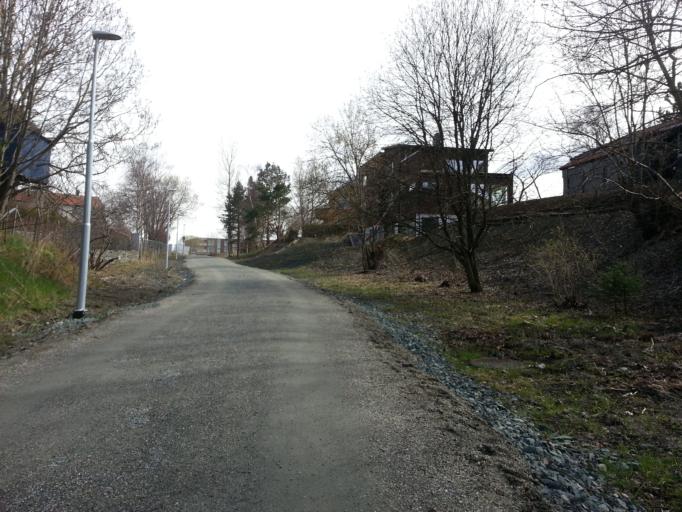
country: NO
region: Sor-Trondelag
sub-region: Trondheim
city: Trondheim
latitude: 63.4138
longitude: 10.4290
